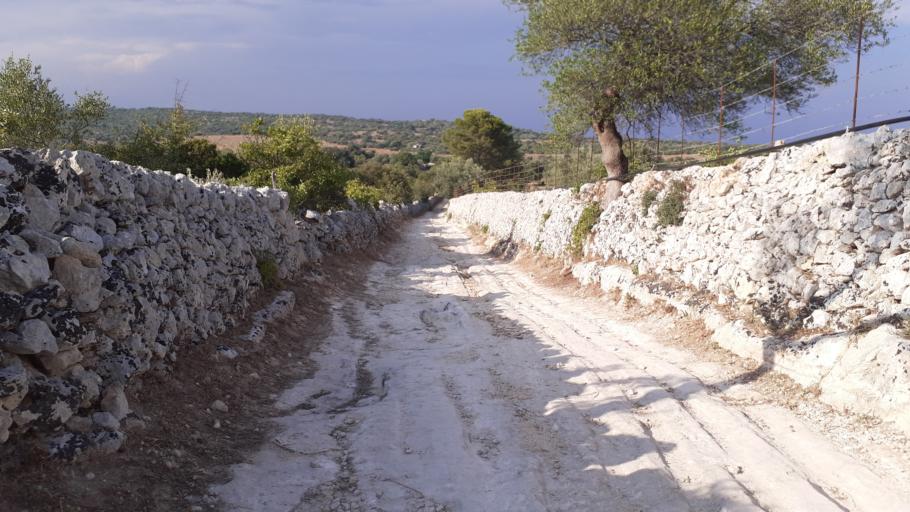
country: IT
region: Sicily
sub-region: Provincia di Siracusa
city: Canicattini Bagni
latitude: 36.9809
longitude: 15.0921
